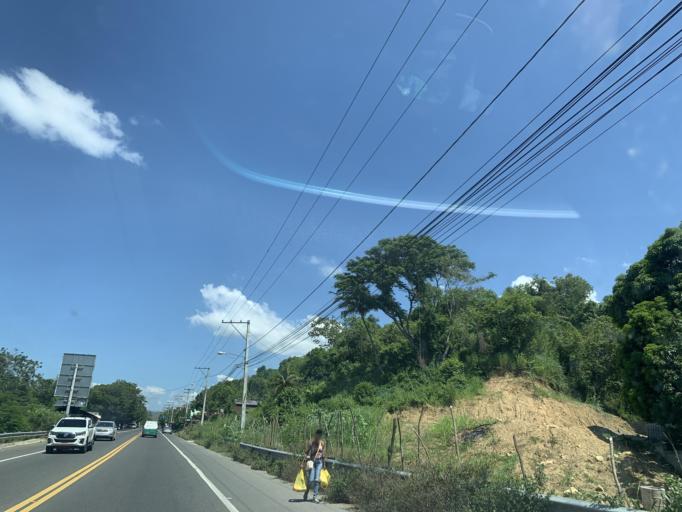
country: DO
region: Puerto Plata
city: Imbert
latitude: 19.7347
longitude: -70.8341
